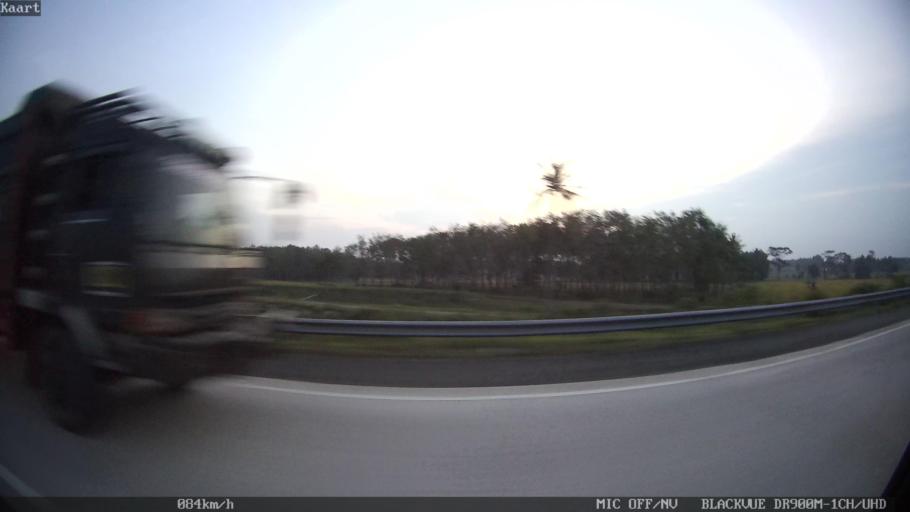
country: ID
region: Lampung
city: Sidorejo
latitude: -5.5827
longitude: 105.5435
